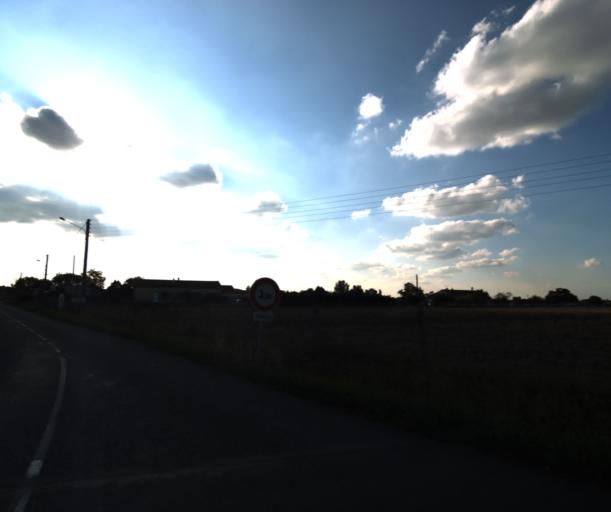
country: FR
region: Midi-Pyrenees
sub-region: Departement de la Haute-Garonne
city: Labastidette
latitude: 43.4773
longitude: 1.2600
